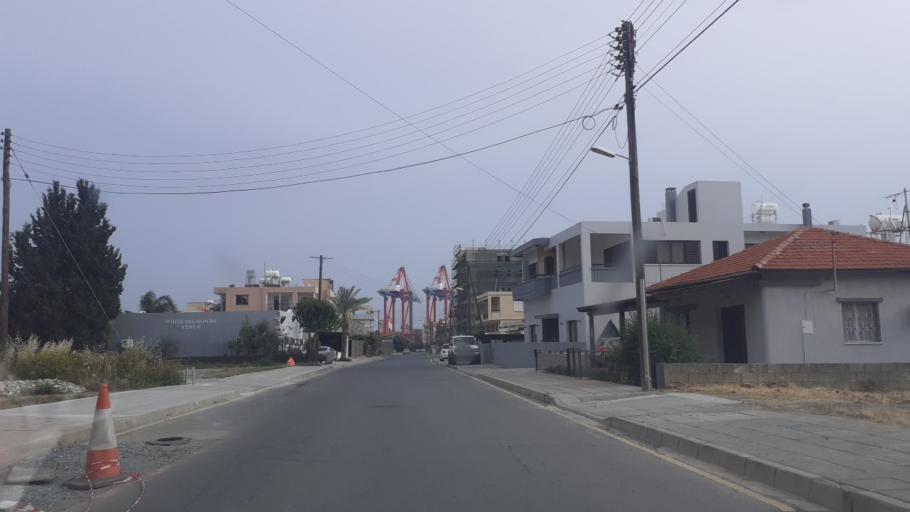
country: CY
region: Limassol
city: Limassol
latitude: 34.6551
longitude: 33.0055
